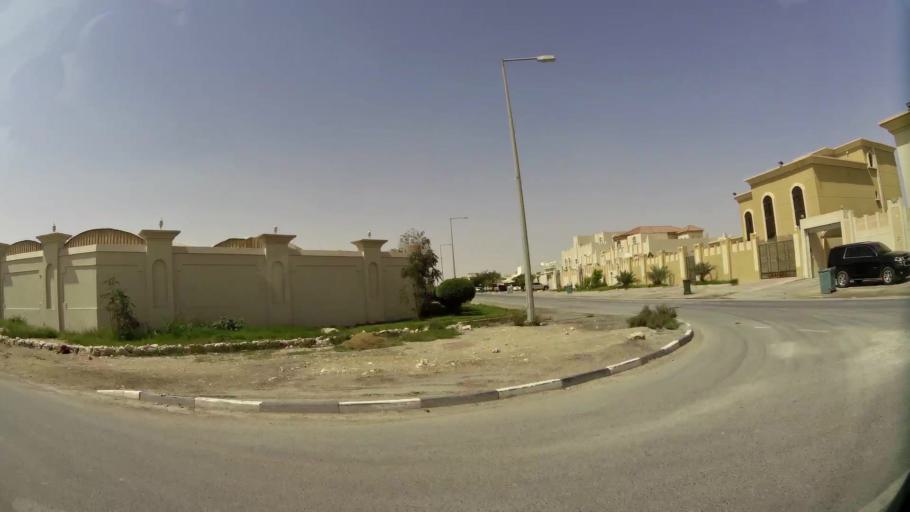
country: QA
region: Baladiyat Umm Salal
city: Umm Salal Muhammad
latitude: 25.3754
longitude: 51.4268
